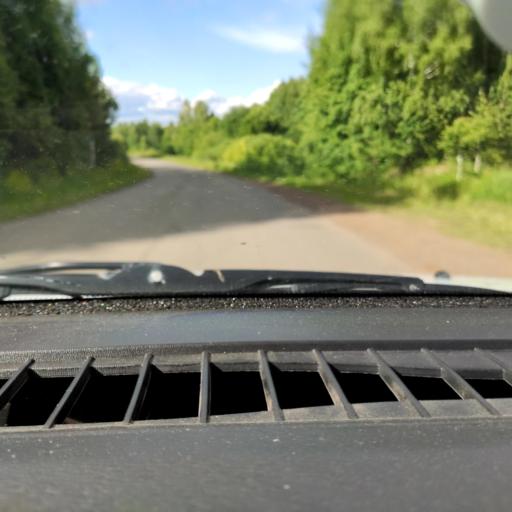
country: RU
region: Perm
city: Uinskoye
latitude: 57.1506
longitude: 56.5712
